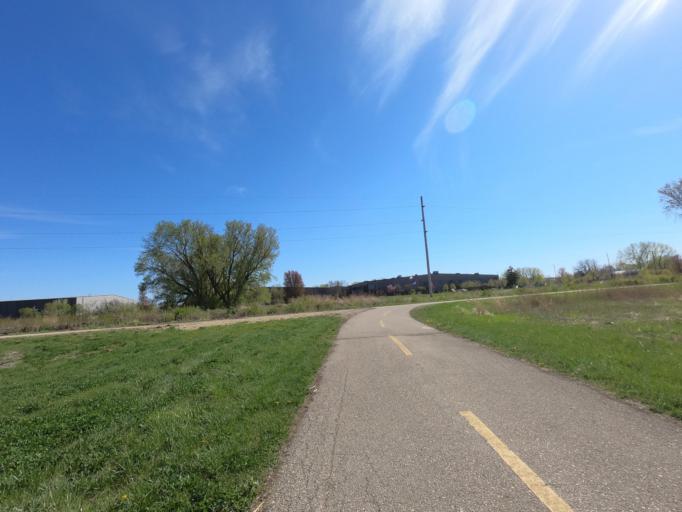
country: US
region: Wisconsin
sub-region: Dane County
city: Middleton
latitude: 43.1043
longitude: -89.5288
